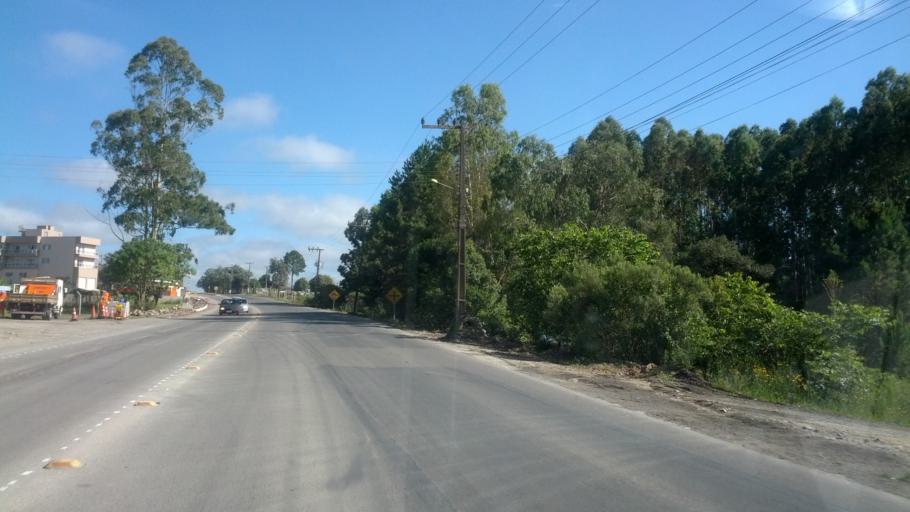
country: BR
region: Santa Catarina
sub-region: Otacilio Costa
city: Otacilio Costa
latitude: -27.4848
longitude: -50.1174
